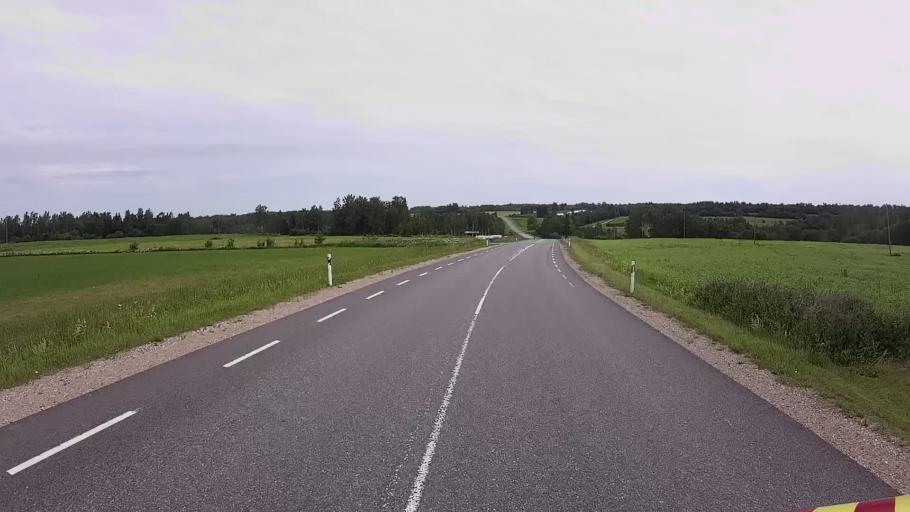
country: EE
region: Viljandimaa
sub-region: Karksi vald
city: Karksi-Nuia
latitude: 58.1430
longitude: 25.5879
